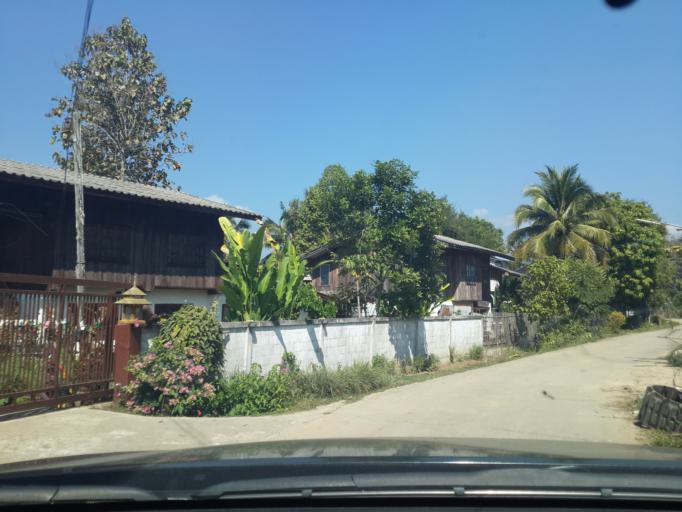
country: TH
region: Chiang Mai
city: San Sai
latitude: 18.8872
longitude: 99.1157
